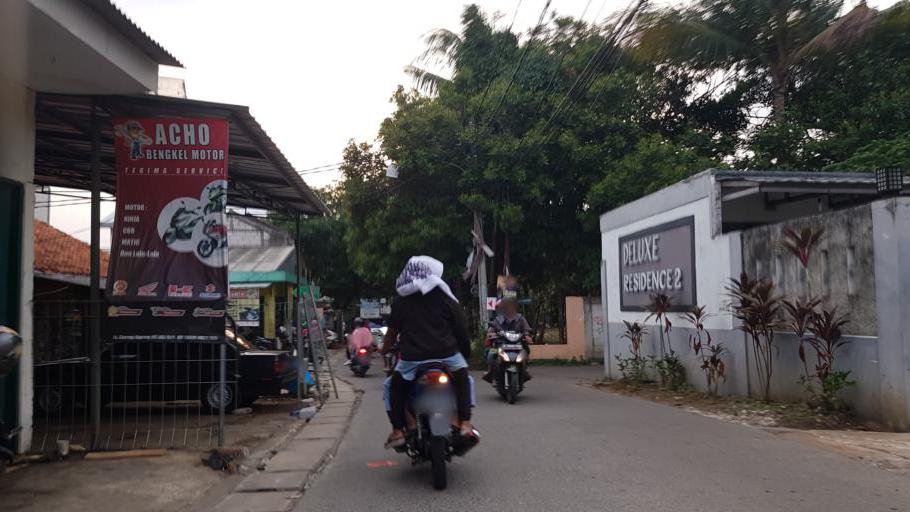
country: ID
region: West Java
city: Depok
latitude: -6.3710
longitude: 106.7988
